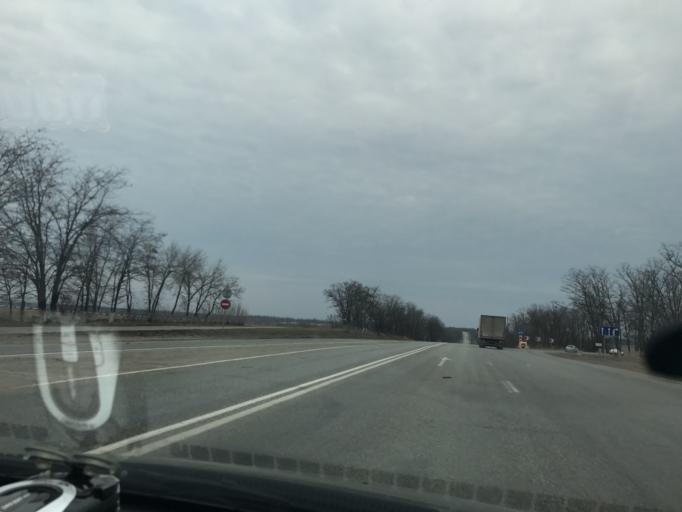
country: RU
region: Krasnodarskiy
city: Kropotkin
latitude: 45.4573
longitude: 40.5230
